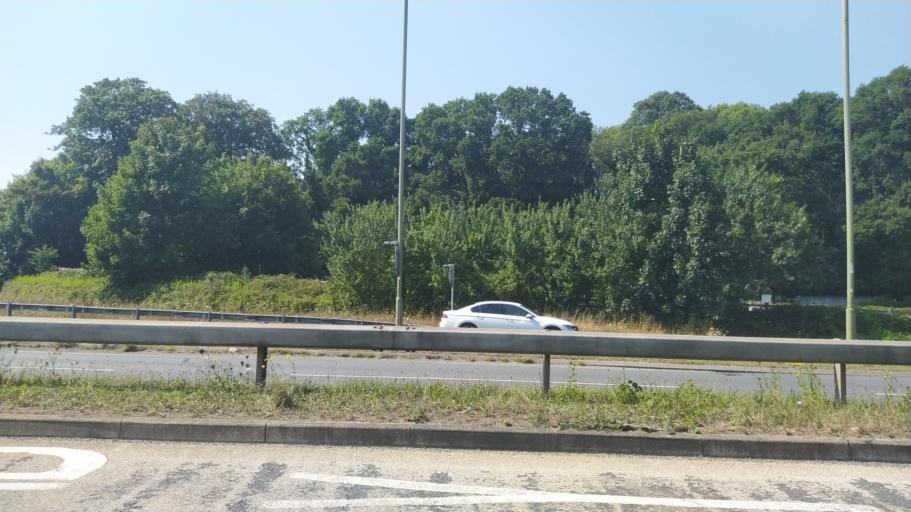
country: GB
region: England
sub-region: Hampshire
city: Totton
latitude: 50.9044
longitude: -1.5002
